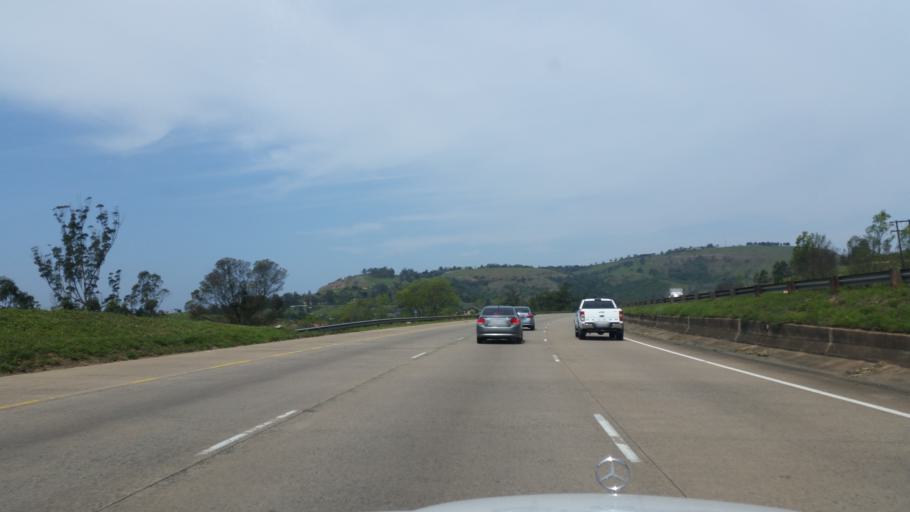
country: ZA
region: KwaZulu-Natal
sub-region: eThekwini Metropolitan Municipality
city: Mpumalanga
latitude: -29.7366
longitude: 30.6479
